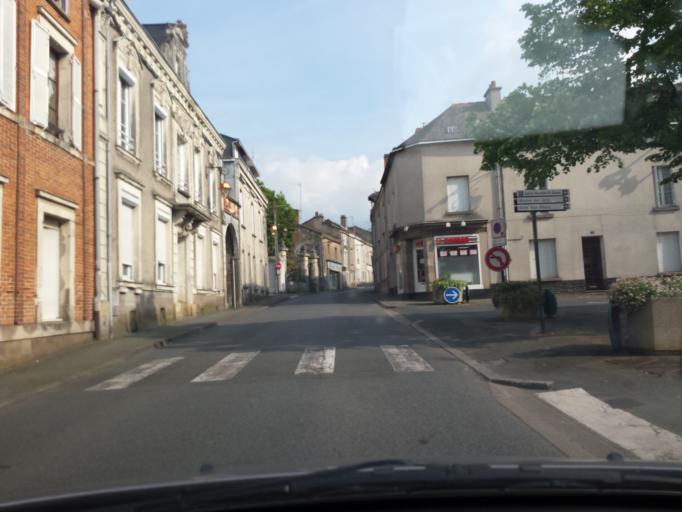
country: FR
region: Pays de la Loire
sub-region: Departement de Maine-et-Loire
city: Chemille-Melay
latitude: 47.2123
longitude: -0.7304
